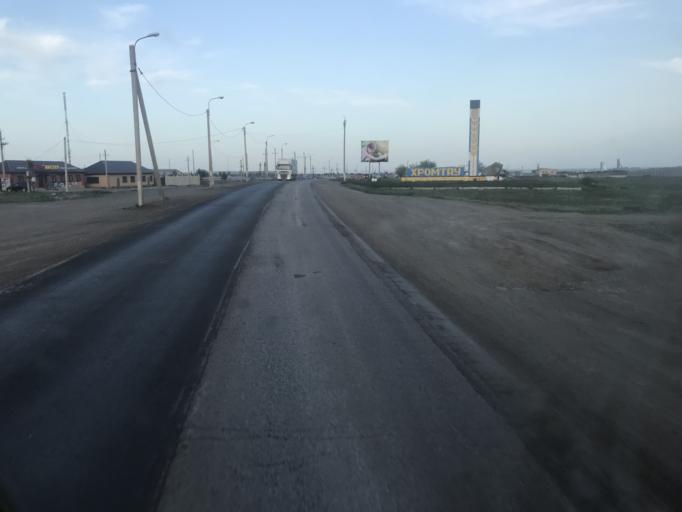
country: KZ
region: Aqtoebe
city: Khromtau
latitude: 50.2585
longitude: 58.4095
